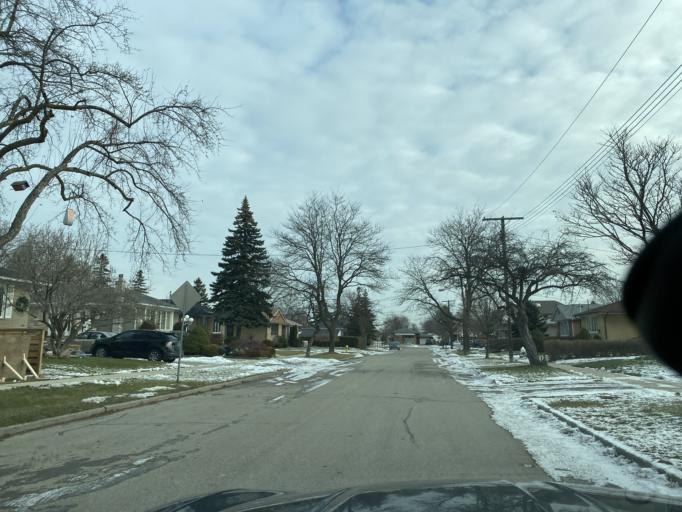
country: CA
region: Ontario
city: Etobicoke
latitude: 43.6635
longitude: -79.5792
